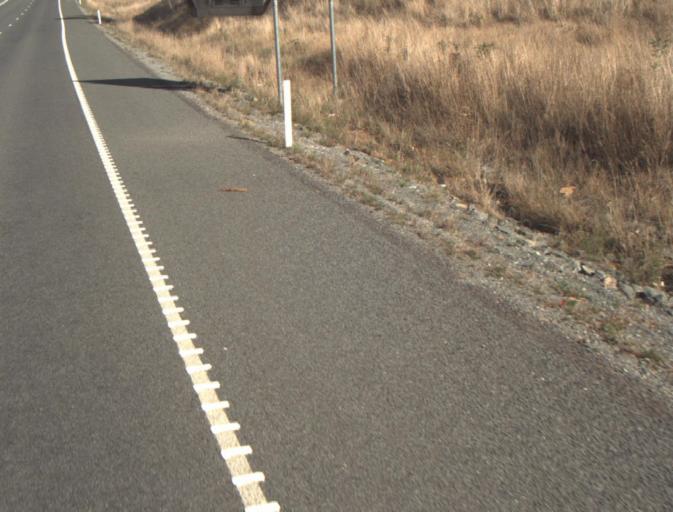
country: AU
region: Tasmania
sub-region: Launceston
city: Mayfield
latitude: -41.3595
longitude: 147.1064
